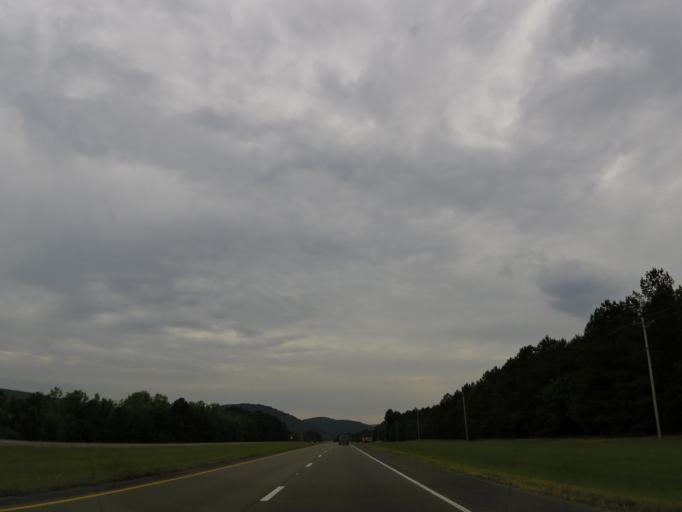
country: US
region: Alabama
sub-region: Jackson County
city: Scottsboro
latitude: 34.6229
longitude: -86.0888
